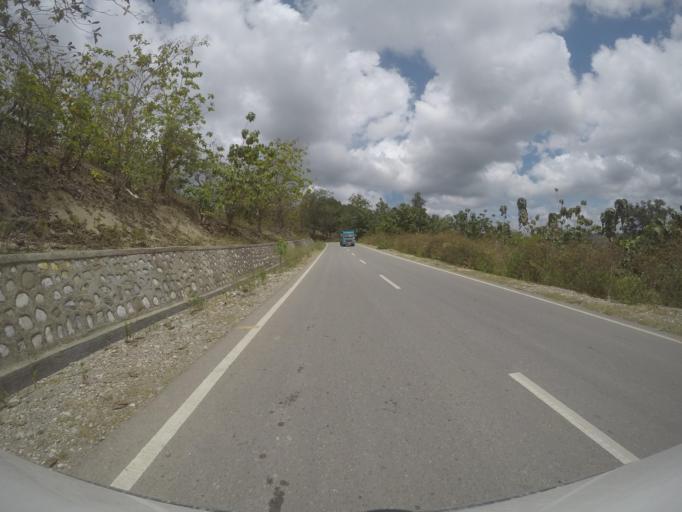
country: TL
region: Viqueque
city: Viqueque
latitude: -8.8748
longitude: 126.3764
